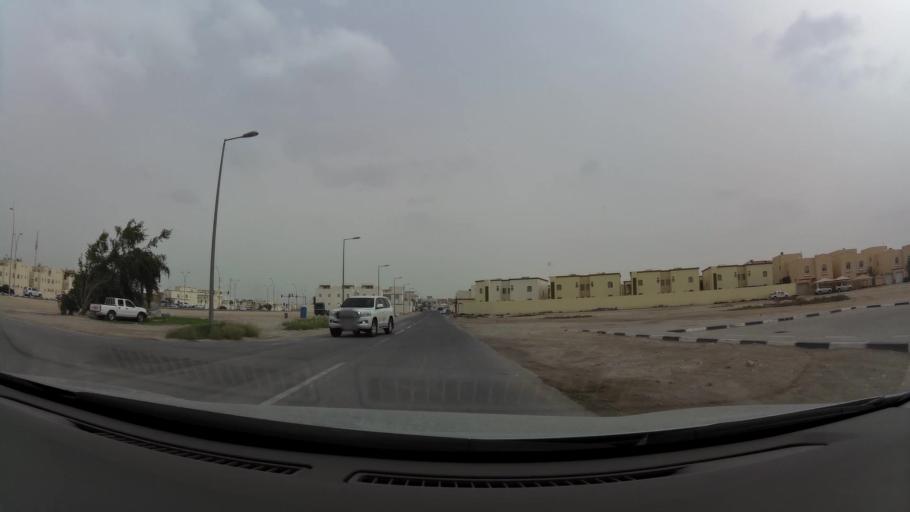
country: QA
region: Baladiyat ad Dawhah
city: Doha
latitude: 25.2459
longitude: 51.5411
